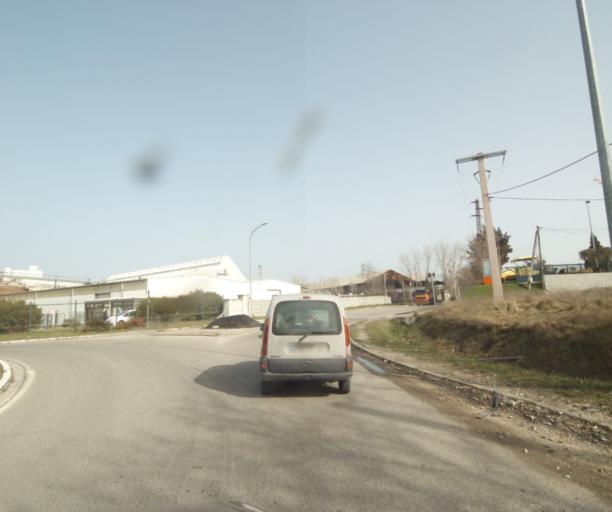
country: FR
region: Provence-Alpes-Cote d'Azur
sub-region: Departement des Bouches-du-Rhone
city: Meyreuil
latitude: 43.4657
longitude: 5.4895
